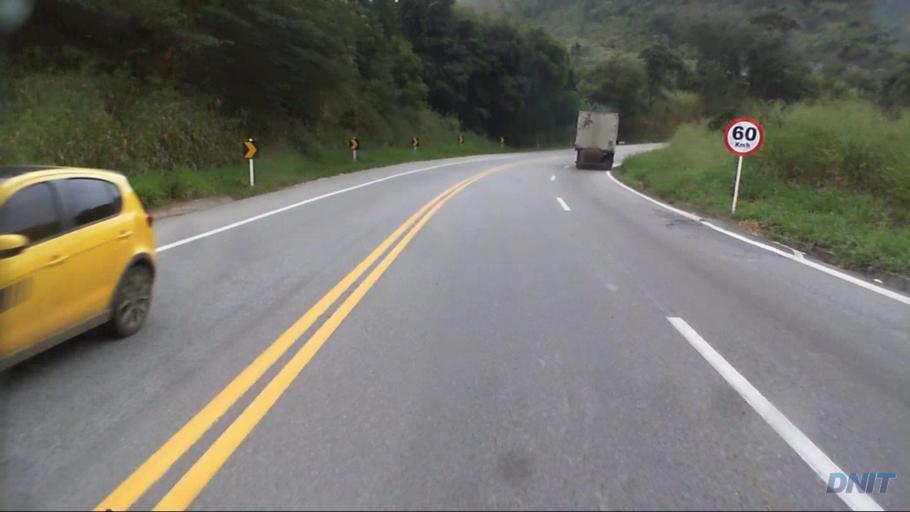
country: BR
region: Minas Gerais
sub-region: Nova Era
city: Nova Era
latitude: -19.6511
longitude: -42.9415
